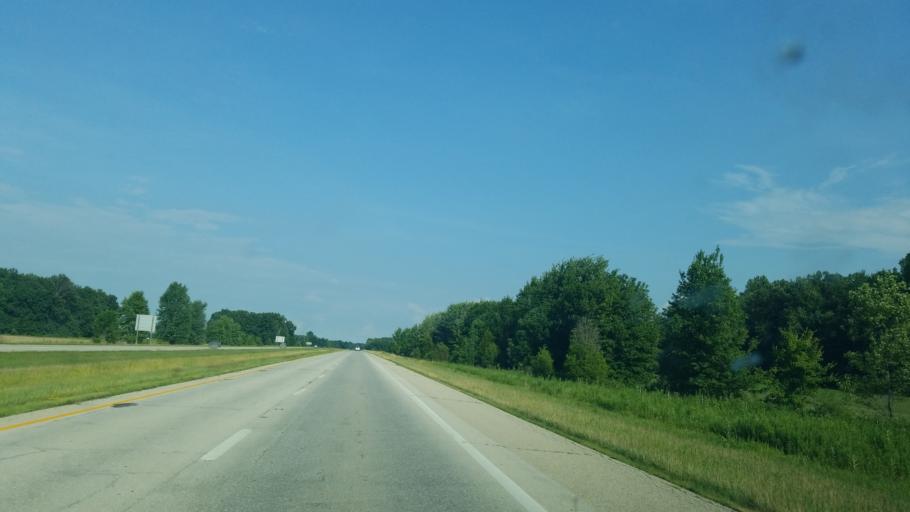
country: US
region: Ohio
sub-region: Brown County
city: Mount Orab
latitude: 39.0350
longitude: -83.9012
